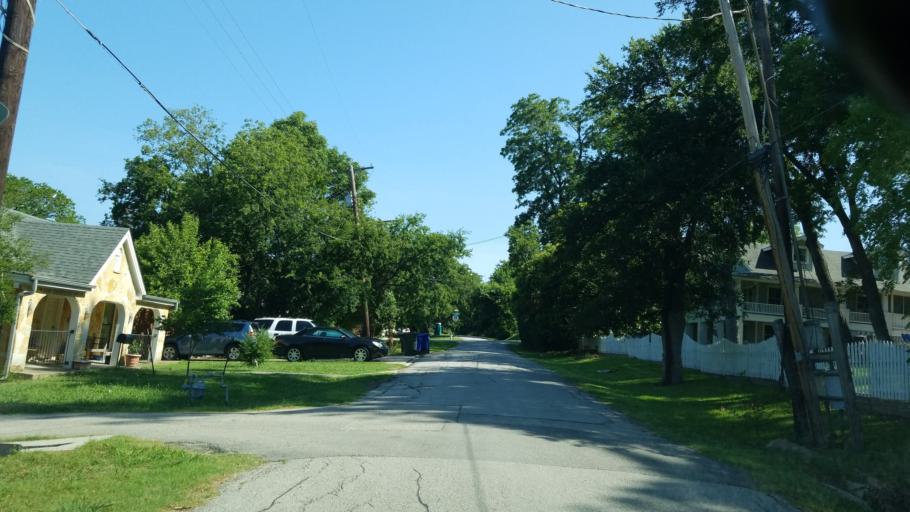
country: US
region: Texas
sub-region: Dallas County
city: Carrollton
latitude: 32.9556
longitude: -96.9031
